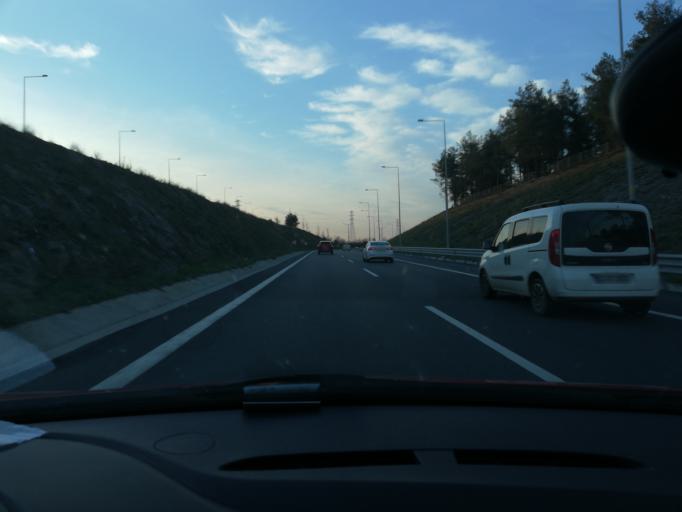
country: TR
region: Istanbul
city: Umraniye
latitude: 41.0528
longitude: 29.1220
